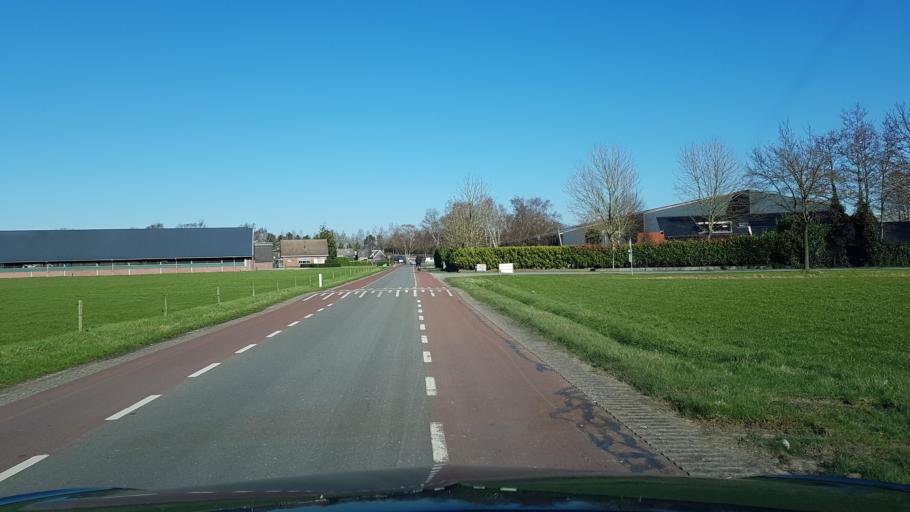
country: NL
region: Gelderland
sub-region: Gemeente Ede
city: Ederveen
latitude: 52.0434
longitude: 5.6006
